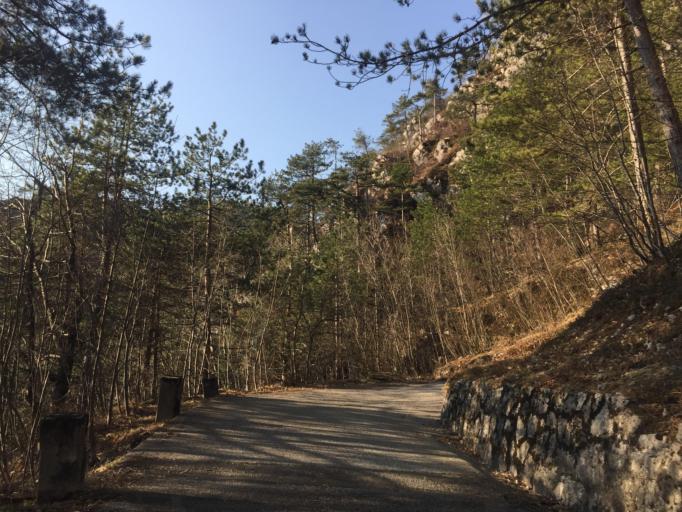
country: IT
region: Friuli Venezia Giulia
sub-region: Provincia di Udine
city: Amaro
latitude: 46.3884
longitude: 13.0758
